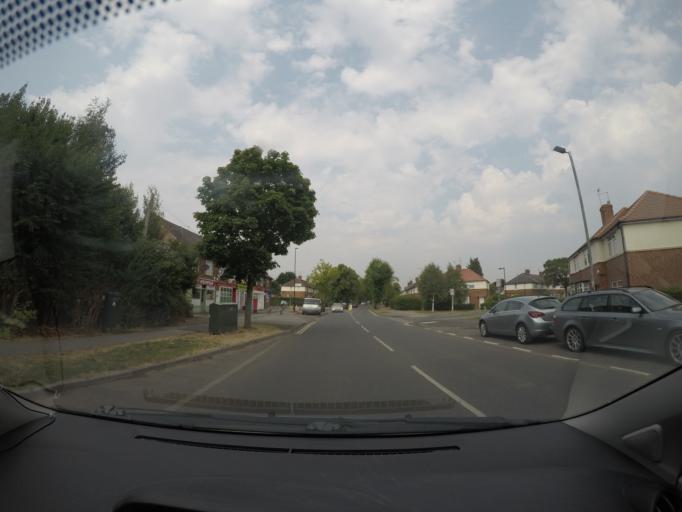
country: GB
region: England
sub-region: City of York
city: Heslington
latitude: 53.9563
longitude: -1.0590
